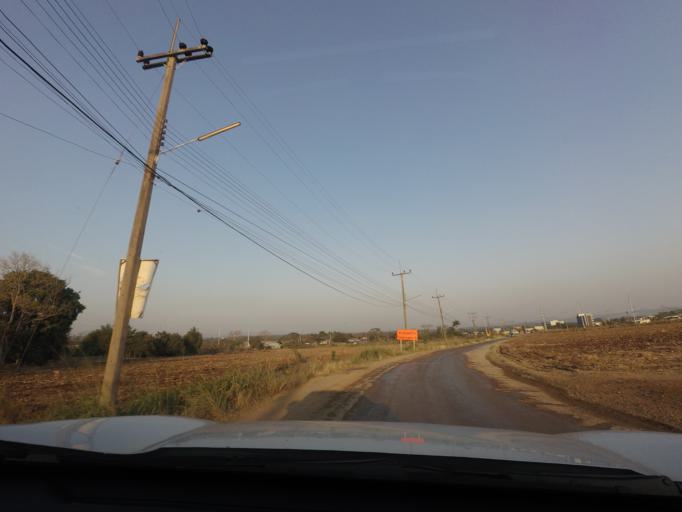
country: TH
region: Nakhon Ratchasima
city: Pak Chong
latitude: 14.6435
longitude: 101.4054
